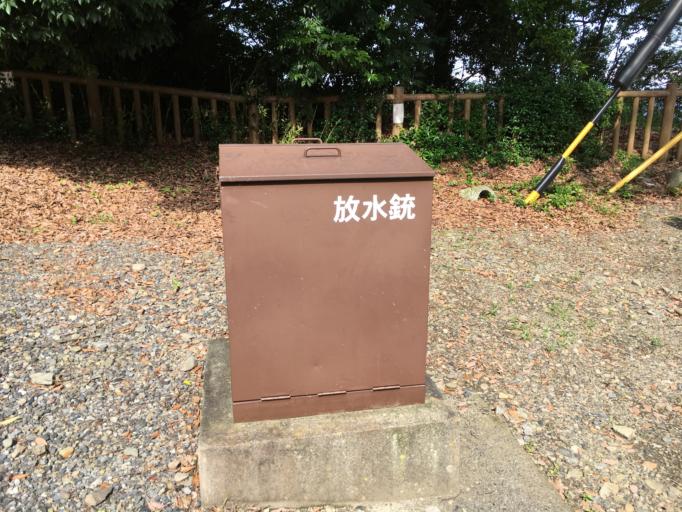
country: JP
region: Shizuoka
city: Shizuoka-shi
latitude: 34.9634
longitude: 138.4673
